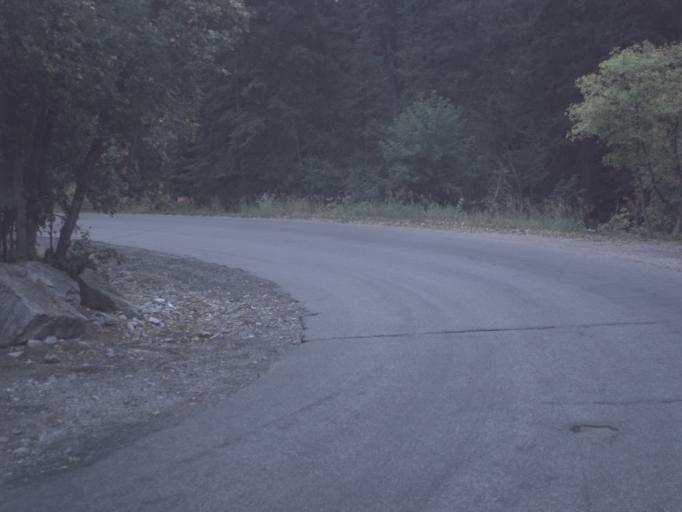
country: US
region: Utah
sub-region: Utah County
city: Lindon
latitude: 40.3943
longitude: -111.5833
